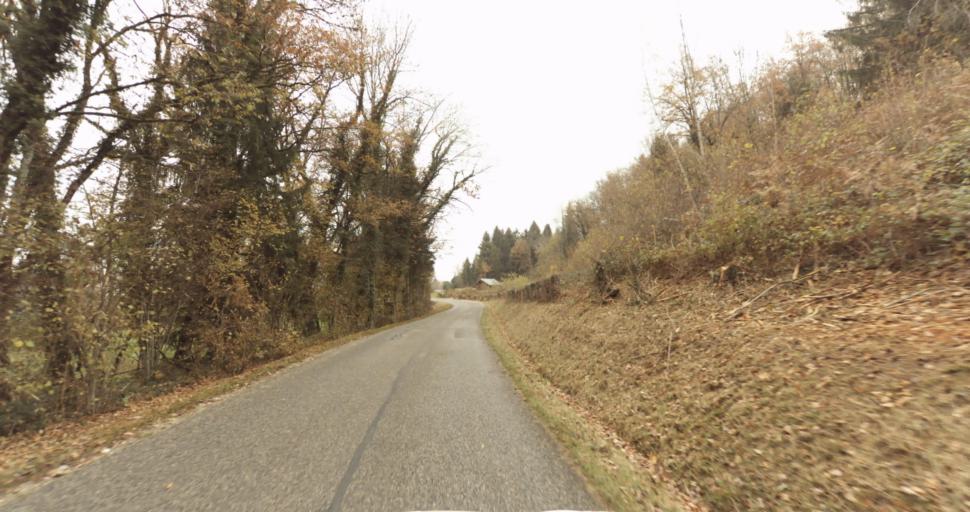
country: FR
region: Rhone-Alpes
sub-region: Departement de la Haute-Savoie
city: Viuz-la-Chiesaz
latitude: 45.8261
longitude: 6.0730
